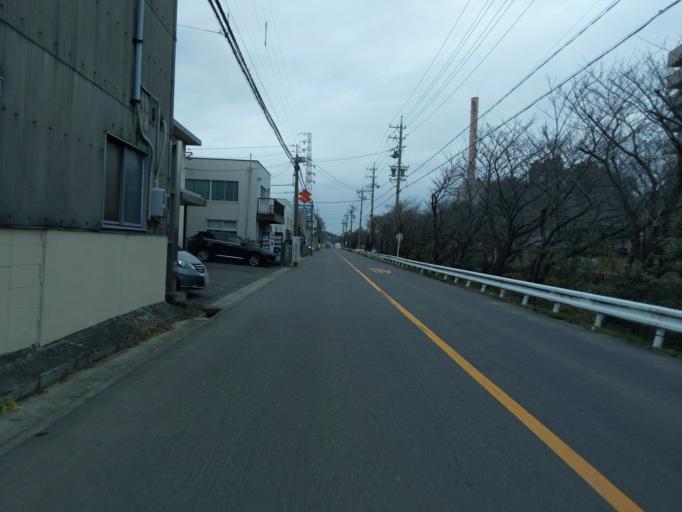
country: JP
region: Aichi
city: Kasugai
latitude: 35.2705
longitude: 136.9680
